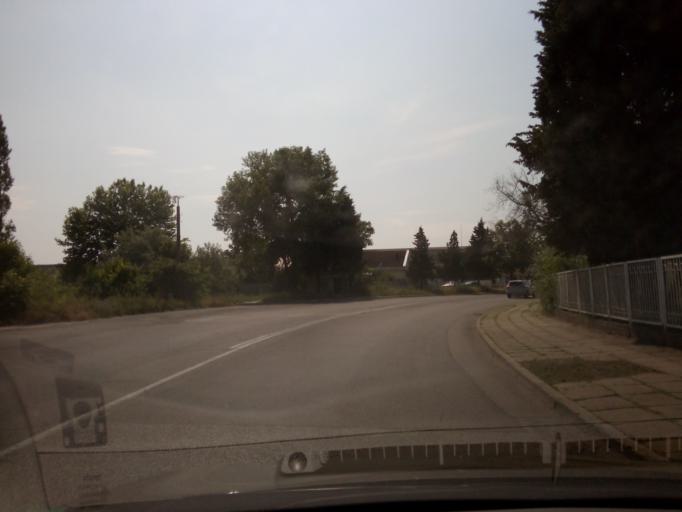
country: BG
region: Burgas
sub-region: Obshtina Pomorie
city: Pomorie
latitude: 42.5689
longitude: 27.6177
